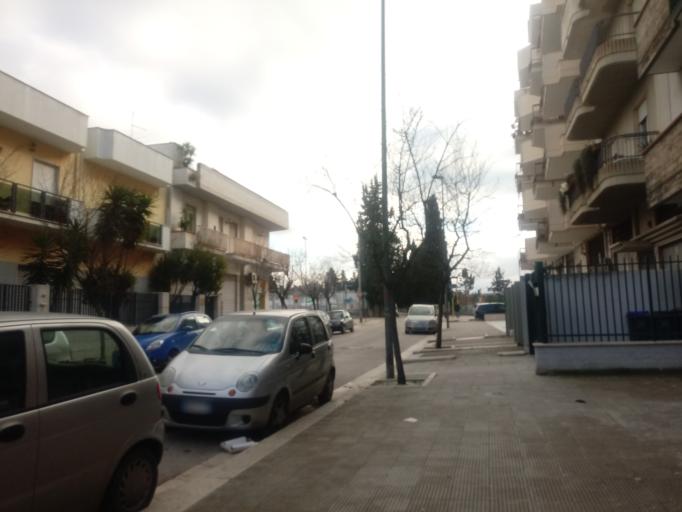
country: IT
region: Apulia
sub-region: Provincia di Barletta - Andria - Trani
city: Andria
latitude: 41.2186
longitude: 16.2995
